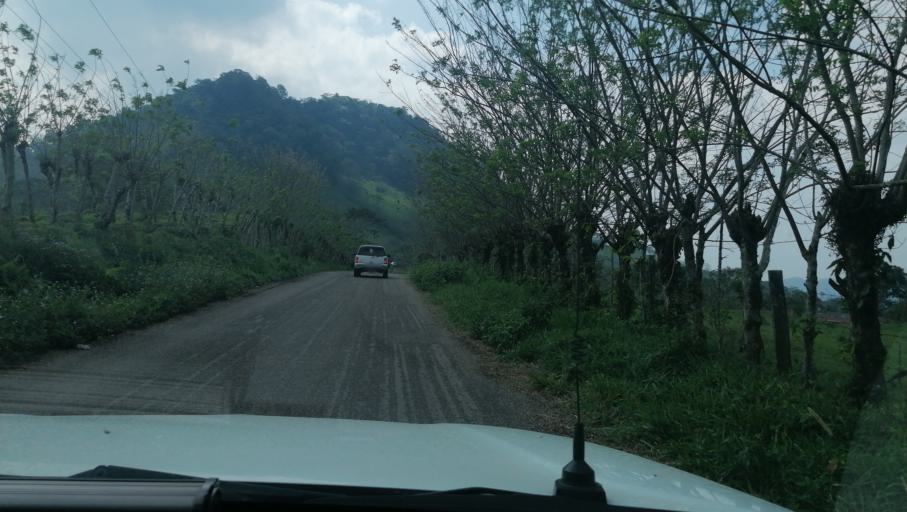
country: MX
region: Chiapas
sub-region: Francisco Leon
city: San Miguel la Sardina
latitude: 17.2302
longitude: -93.3512
